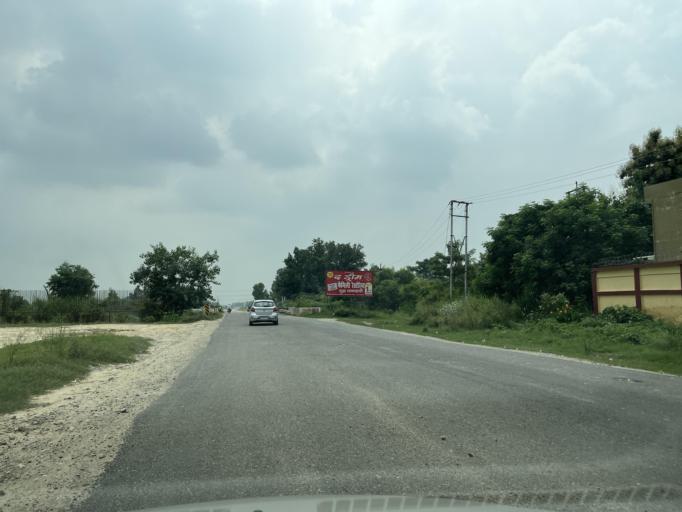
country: IN
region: Uttar Pradesh
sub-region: Bijnor
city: Najibabad
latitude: 29.5733
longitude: 78.3386
